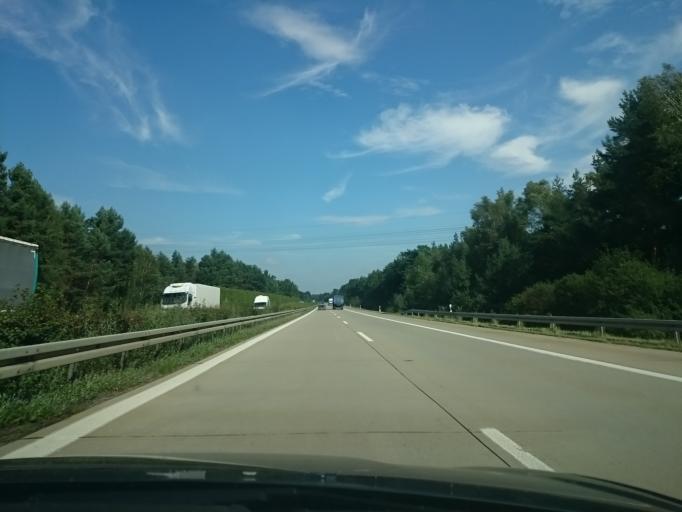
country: DE
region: Brandenburg
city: Schipkau
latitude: 51.5055
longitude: 13.9034
